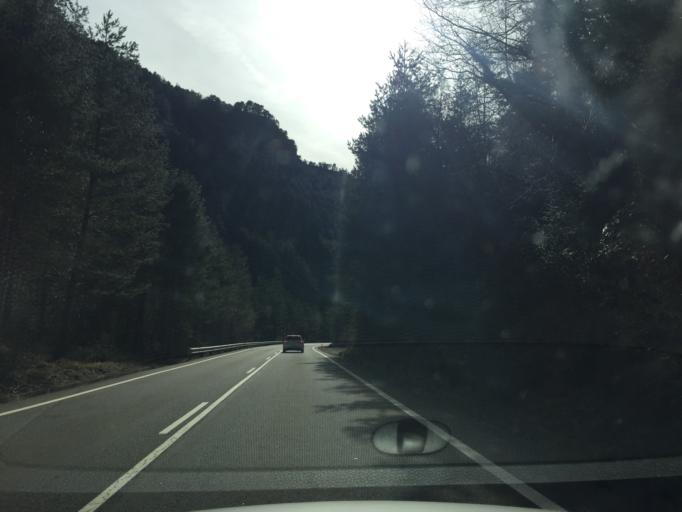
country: ES
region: Aragon
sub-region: Provincia de Huesca
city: Bielsa
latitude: 42.5910
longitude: 0.2332
